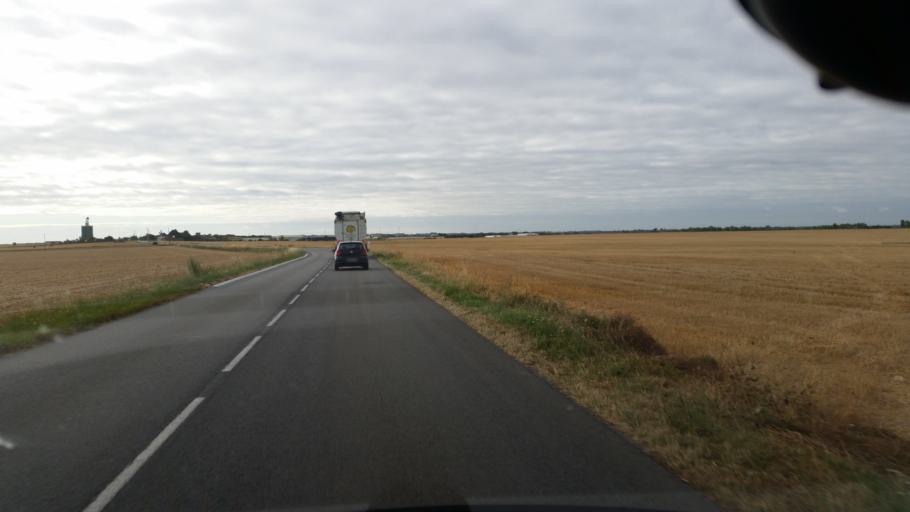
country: FR
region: Poitou-Charentes
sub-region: Departement de la Charente-Maritime
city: Marans
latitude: 46.2942
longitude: -0.9670
